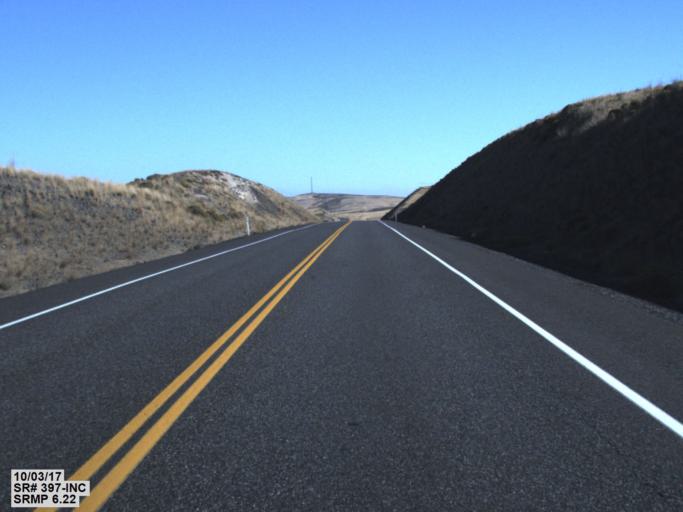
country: US
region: Washington
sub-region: Benton County
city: Highland
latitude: 46.1326
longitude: -119.0861
